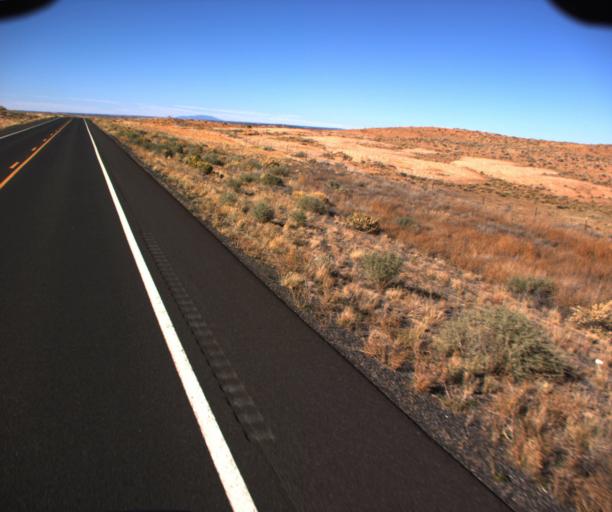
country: US
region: Arizona
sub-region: Coconino County
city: Kaibito
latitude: 36.4768
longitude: -110.7009
